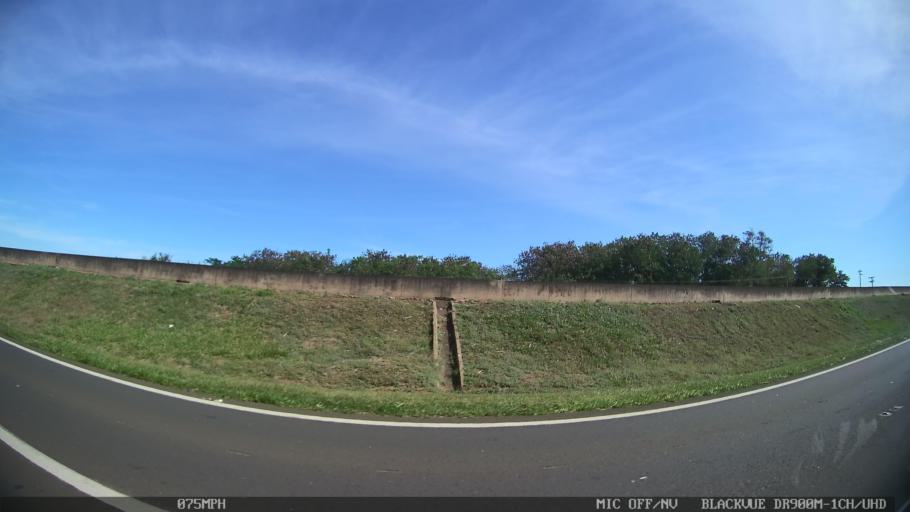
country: BR
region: Sao Paulo
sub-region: Porto Ferreira
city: Porto Ferreira
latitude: -21.8377
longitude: -47.4951
